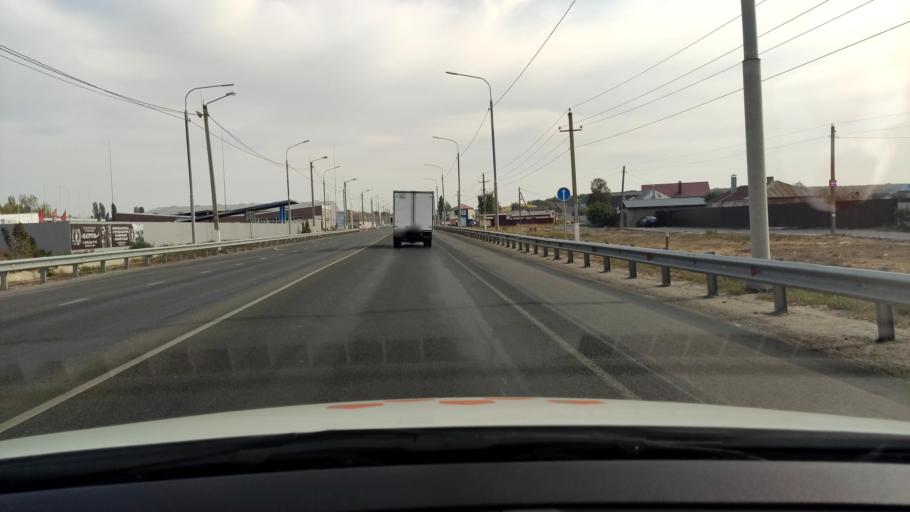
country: RU
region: Voronezj
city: Somovo
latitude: 51.6916
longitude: 39.3704
